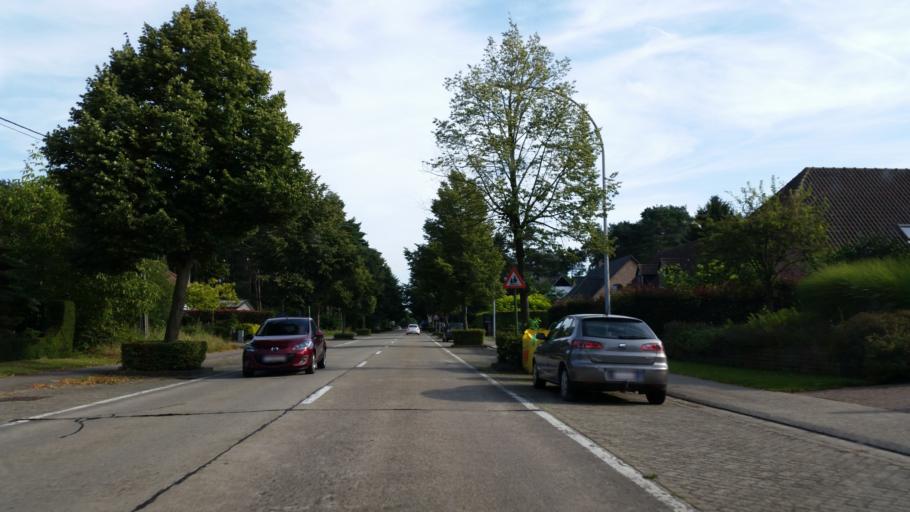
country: BE
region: Flanders
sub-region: Provincie Antwerpen
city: Westerlo
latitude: 51.0967
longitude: 4.9192
